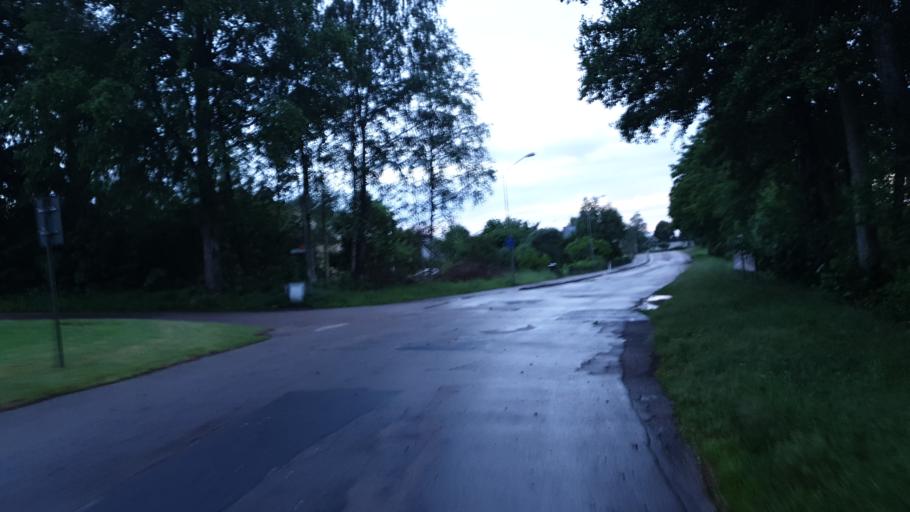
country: SE
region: Kronoberg
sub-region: Ljungby Kommun
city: Ljungby
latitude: 56.8339
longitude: 13.9644
